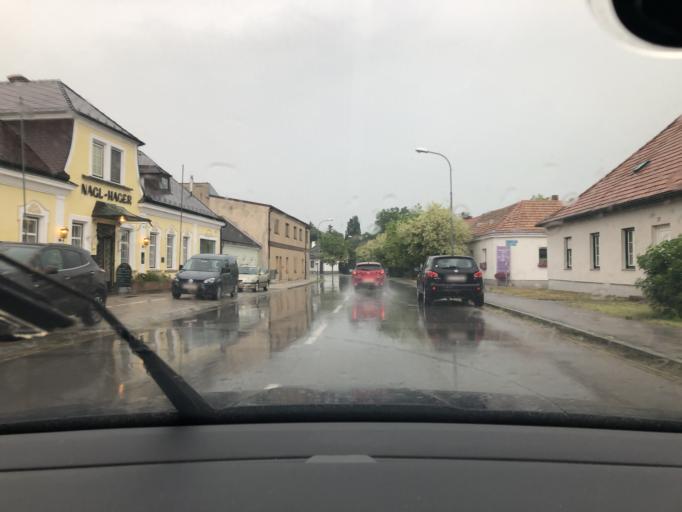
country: AT
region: Lower Austria
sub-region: Politischer Bezirk Ganserndorf
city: Marchegg
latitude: 48.2765
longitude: 16.9100
